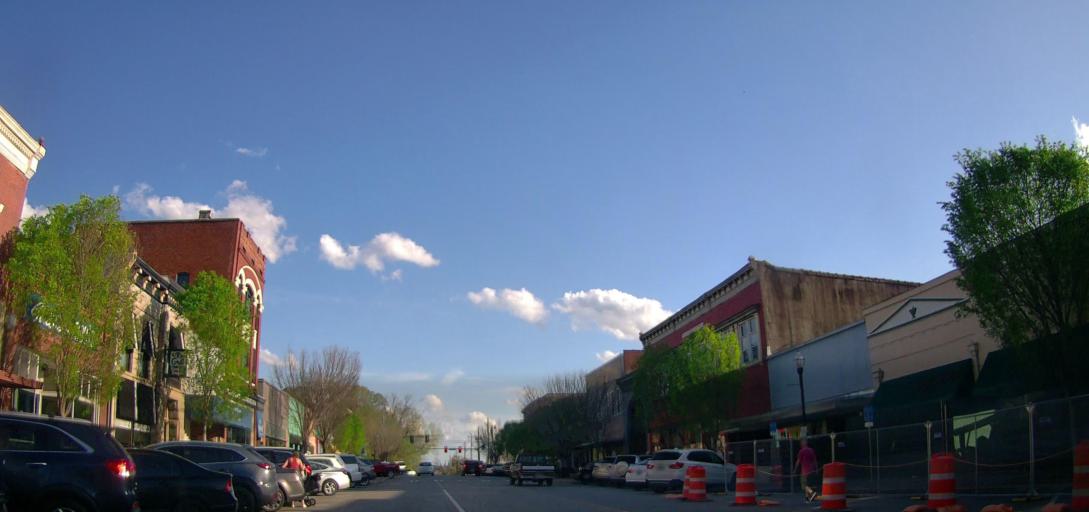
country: US
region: Georgia
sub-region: Baldwin County
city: Milledgeville
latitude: 33.0808
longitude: -83.2270
